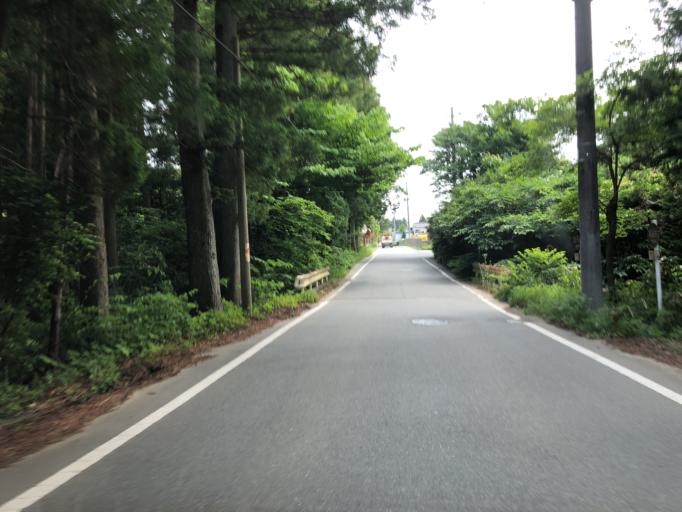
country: JP
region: Fukushima
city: Namie
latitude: 37.3014
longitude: 140.9996
